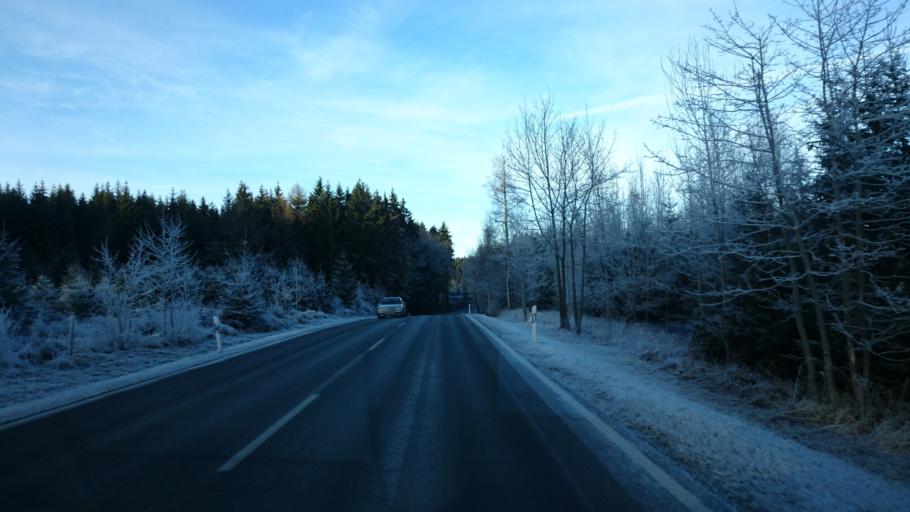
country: DE
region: Thuringia
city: Schleiz
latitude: 50.5490
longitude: 11.8456
